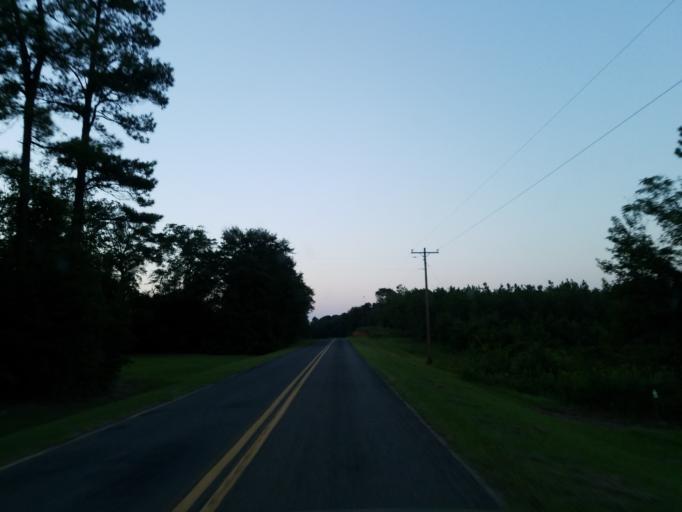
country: US
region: Georgia
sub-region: Dooly County
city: Unadilla
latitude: 32.2267
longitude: -83.7964
